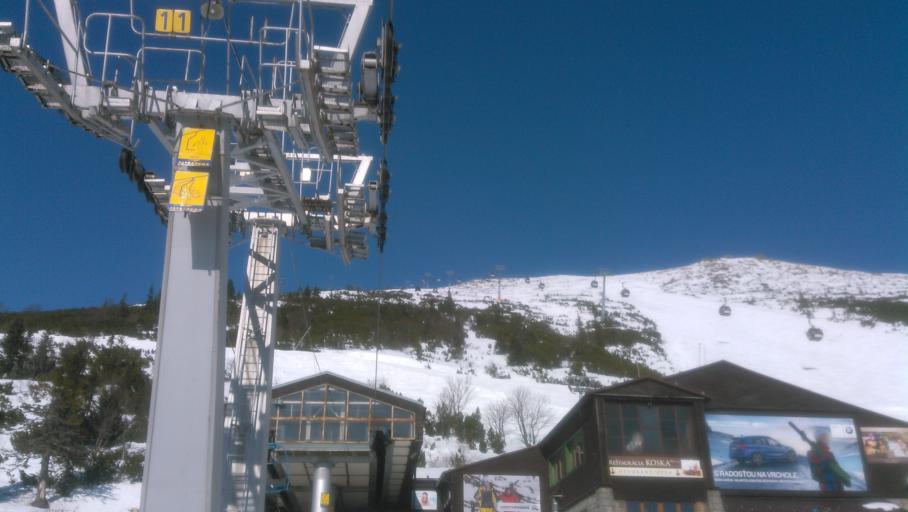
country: SK
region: Banskobystricky
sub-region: Okres Banska Bystrica
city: Brezno
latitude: 48.9321
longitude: 19.5975
